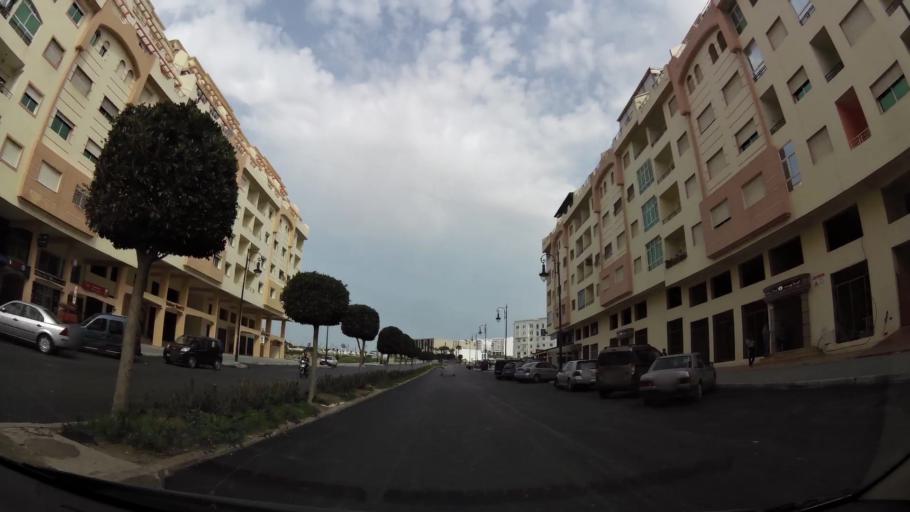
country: MA
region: Tanger-Tetouan
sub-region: Tanger-Assilah
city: Boukhalef
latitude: 35.7372
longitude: -5.8800
